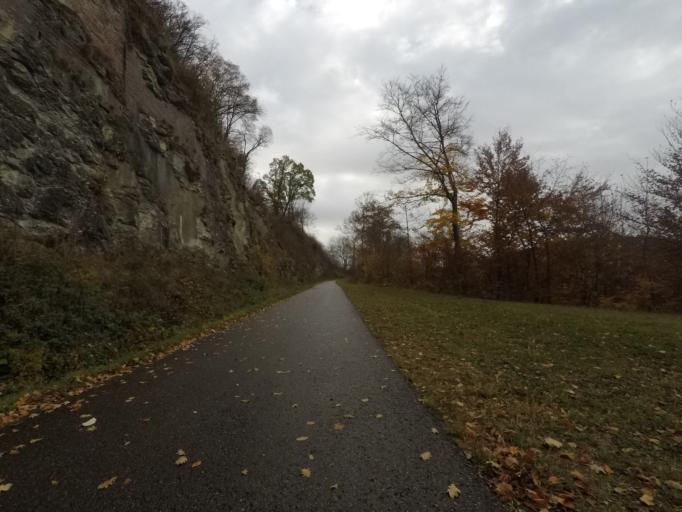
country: DE
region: Baden-Wuerttemberg
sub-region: Tuebingen Region
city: Pfullingen
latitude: 48.4065
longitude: 9.2699
